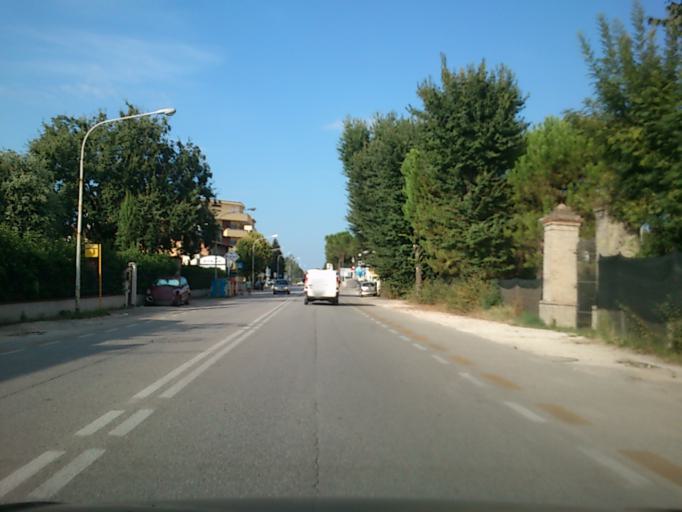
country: IT
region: The Marches
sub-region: Provincia di Pesaro e Urbino
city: Fano
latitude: 43.8345
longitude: 13.0041
